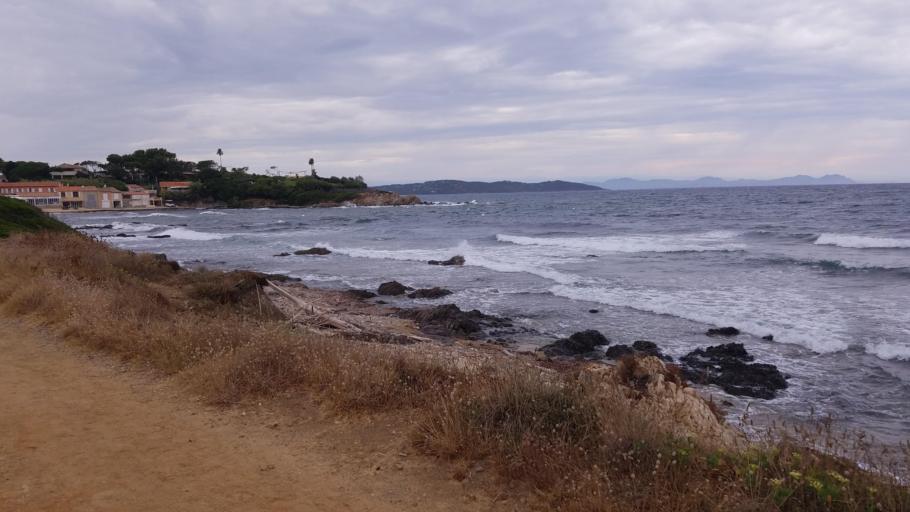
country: FR
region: Provence-Alpes-Cote d'Azur
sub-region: Departement du Var
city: Ramatuelle
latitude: 43.2065
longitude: 6.6690
